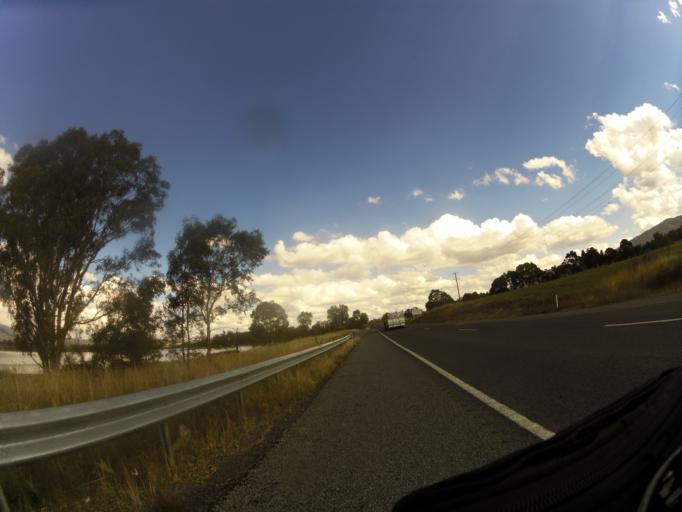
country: AU
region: Victoria
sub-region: Mansfield
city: Mansfield
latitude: -36.9017
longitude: 145.9970
